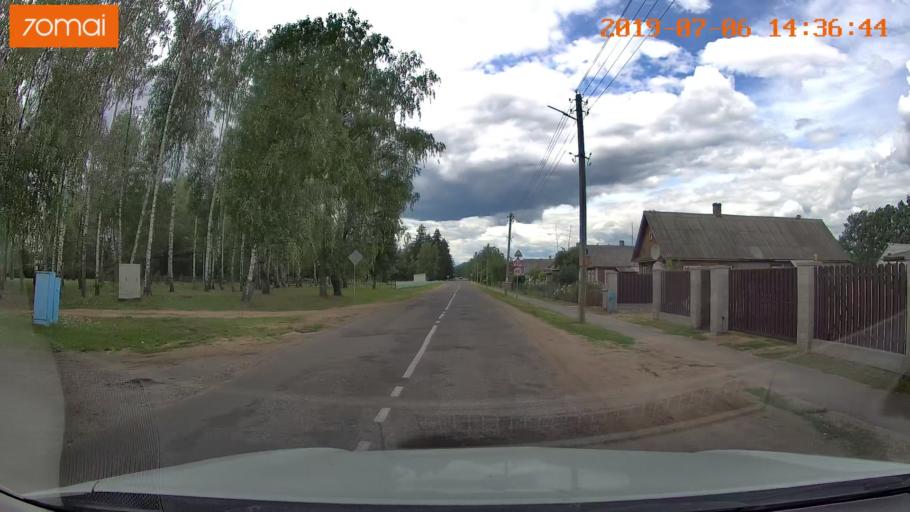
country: BY
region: Minsk
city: Ivyanyets
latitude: 53.8927
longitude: 26.7283
